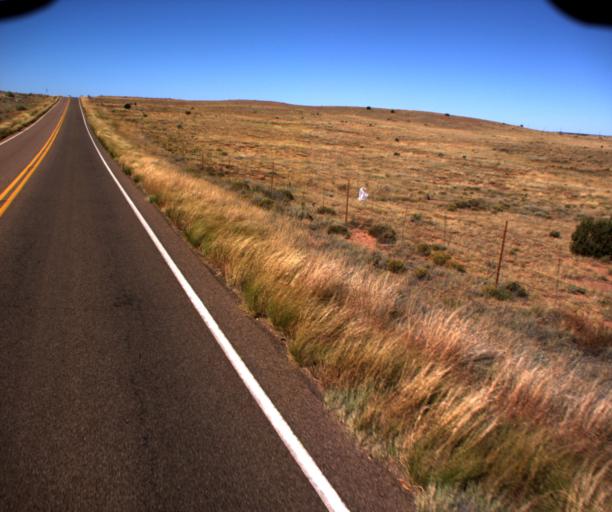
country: US
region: Arizona
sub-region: Navajo County
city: Snowflake
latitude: 34.5129
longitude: -110.1409
